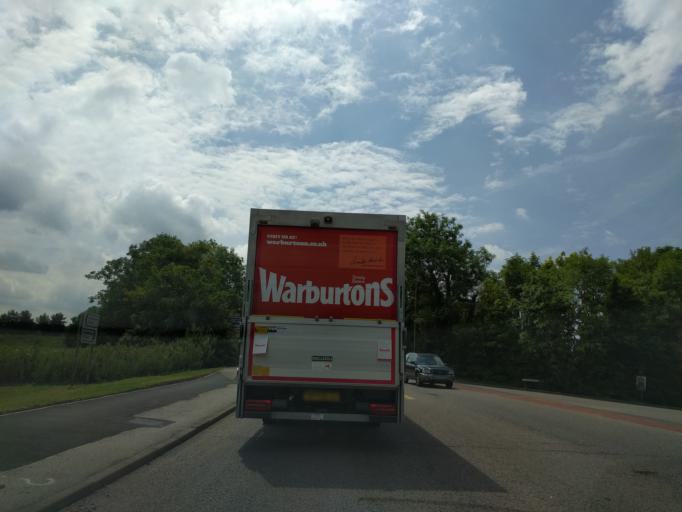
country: GB
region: England
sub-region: Cambridgeshire
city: Histon
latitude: 52.2373
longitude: 0.1118
